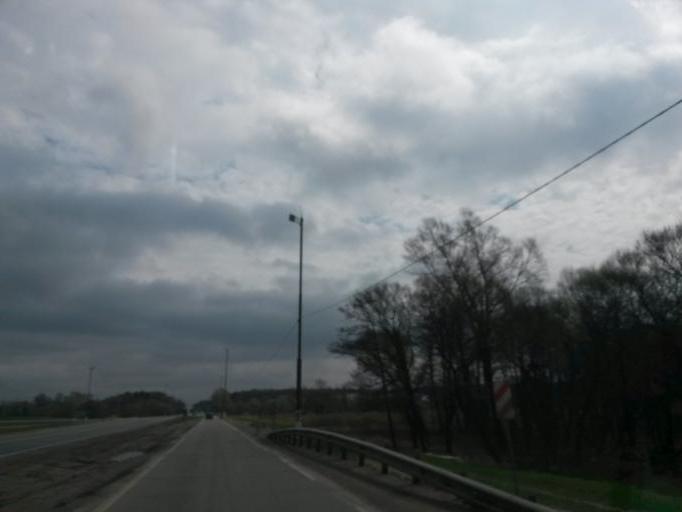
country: RU
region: Moskovskaya
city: L'vovskiy
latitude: 55.3317
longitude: 37.5687
